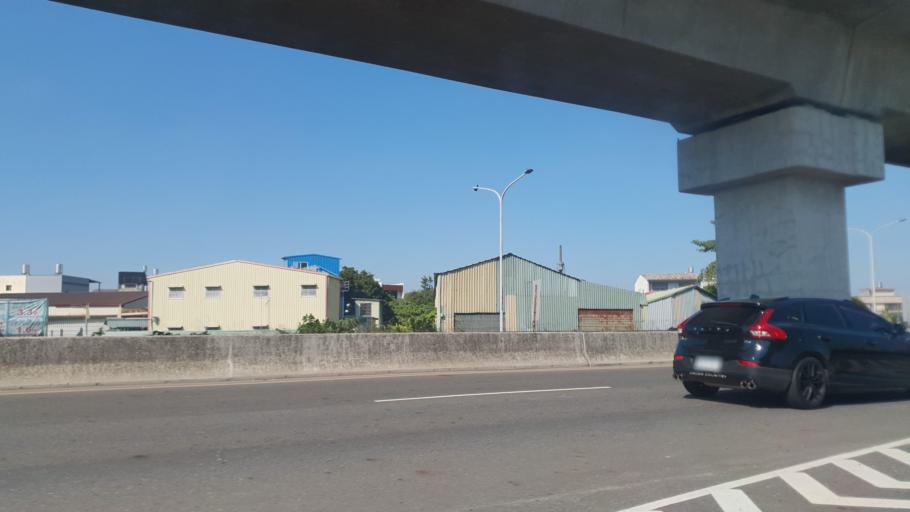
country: TW
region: Taiwan
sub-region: Tainan
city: Tainan
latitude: 23.0215
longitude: 120.2894
